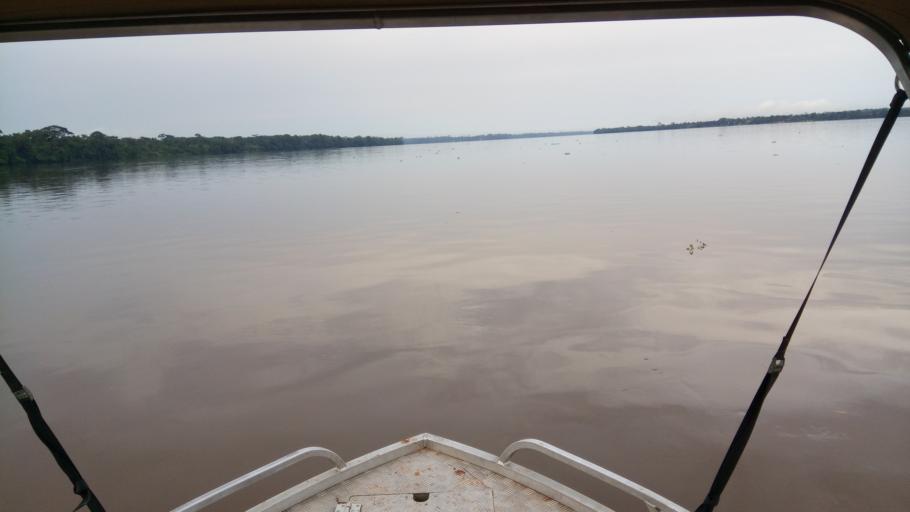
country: CD
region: Eastern Province
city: Kisangani
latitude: 0.5744
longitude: 24.8135
